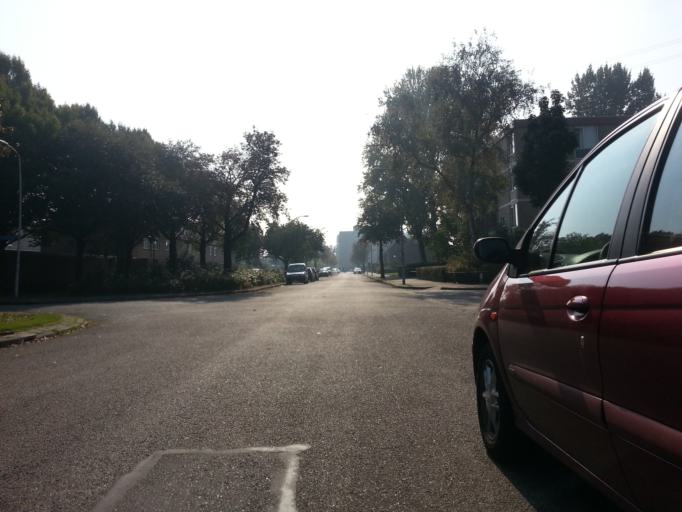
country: NL
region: North Brabant
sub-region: Gemeente Eindhoven
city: Villapark
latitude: 51.4732
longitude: 5.4958
